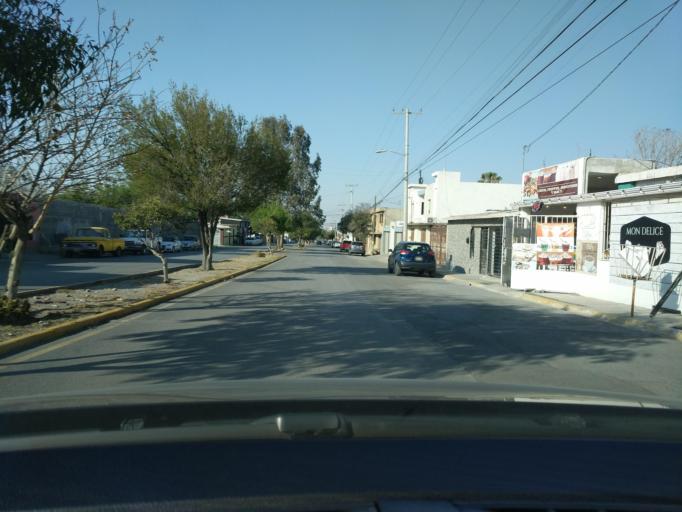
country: MX
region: Coahuila
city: Saltillo
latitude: 25.4645
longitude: -100.9867
